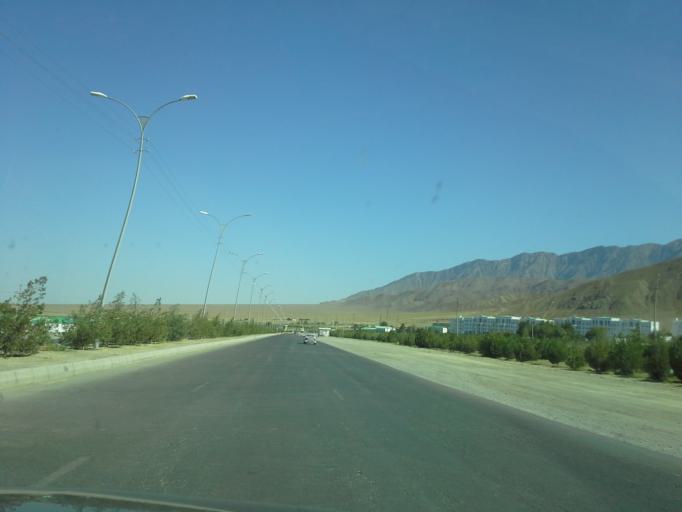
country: TM
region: Ahal
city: Baharly
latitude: 38.5231
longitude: 57.1794
